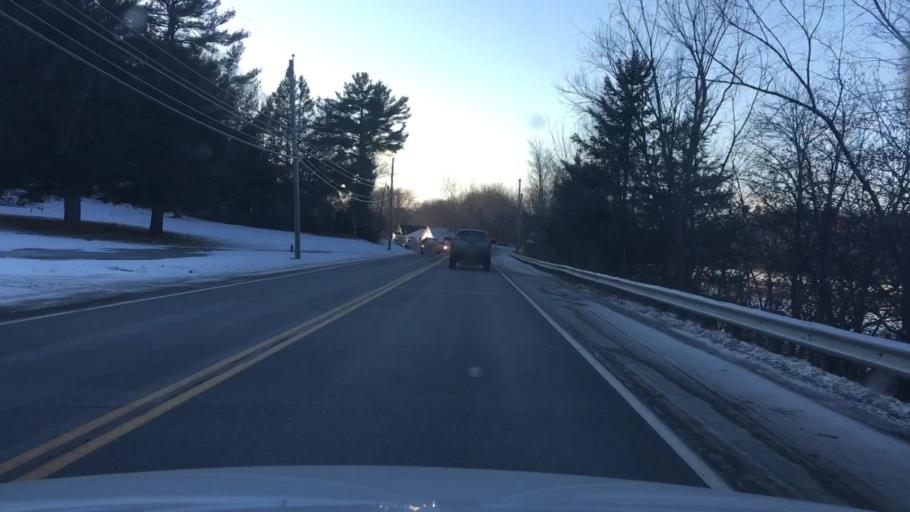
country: US
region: Maine
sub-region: Penobscot County
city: Veazie
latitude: 44.8196
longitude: -68.7149
